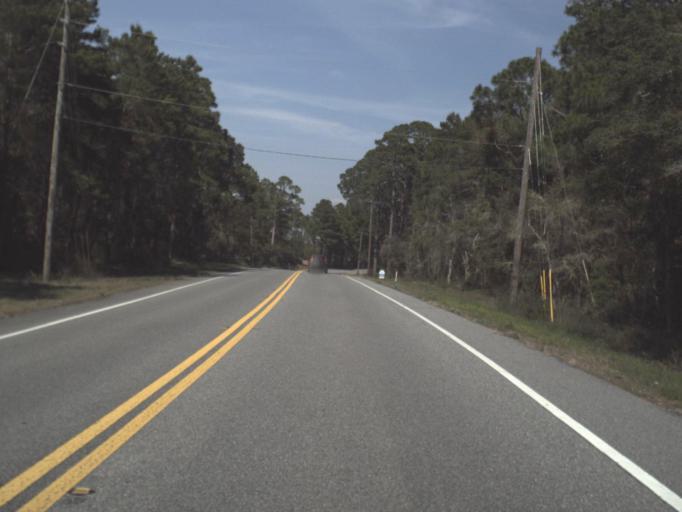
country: US
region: Florida
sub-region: Franklin County
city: Eastpoint
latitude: 29.7866
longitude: -84.7675
